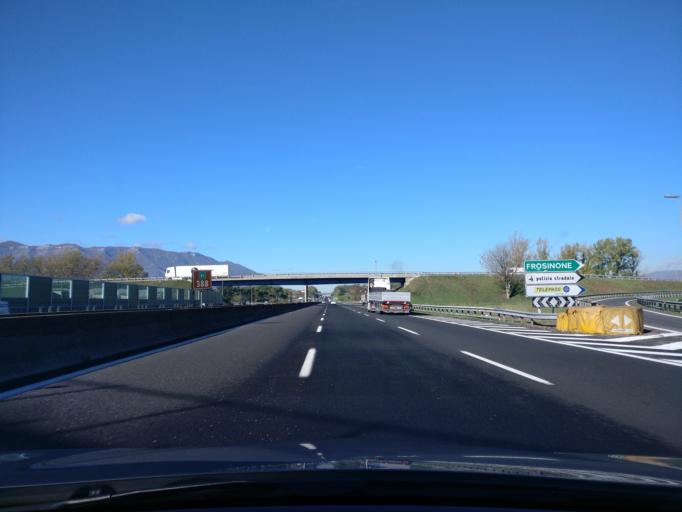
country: IT
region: Latium
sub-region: Provincia di Frosinone
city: Frosinone
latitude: 41.6190
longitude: 13.3142
